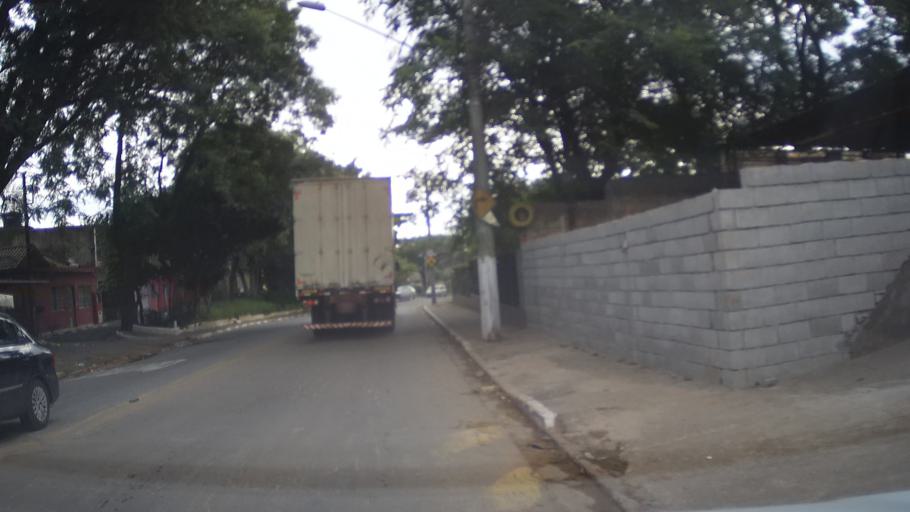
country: BR
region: Sao Paulo
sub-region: Guarulhos
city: Guarulhos
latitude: -23.4159
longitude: -46.4661
